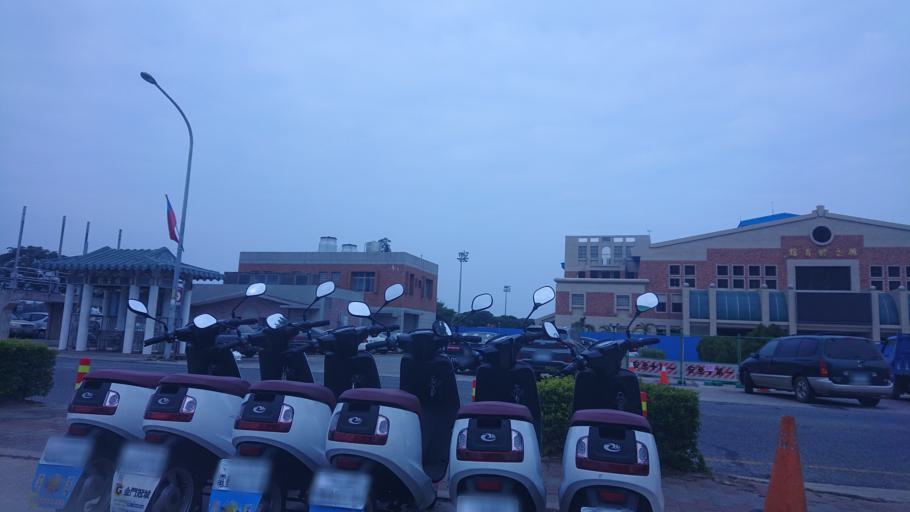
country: TW
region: Fukien
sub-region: Kinmen
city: Jincheng
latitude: 24.4296
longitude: 118.3156
